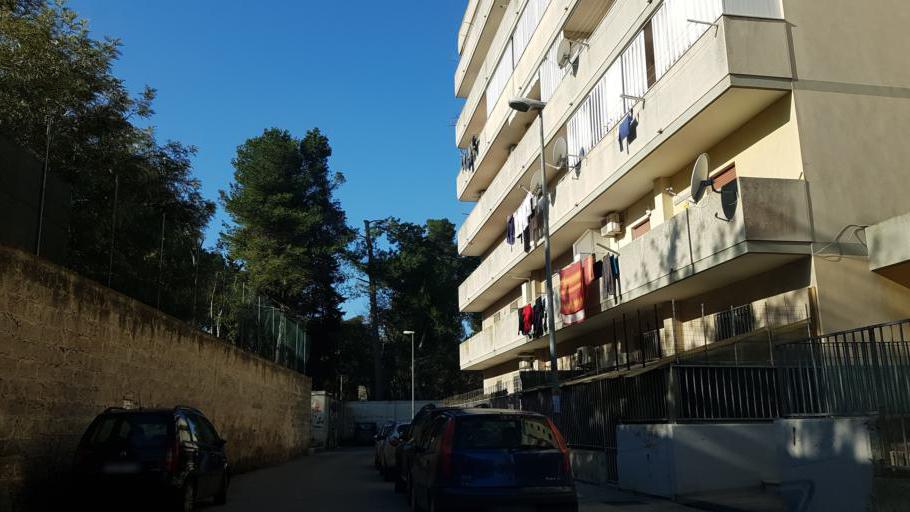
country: IT
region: Apulia
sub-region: Provincia di Brindisi
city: Brindisi
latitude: 40.6290
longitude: 17.9232
